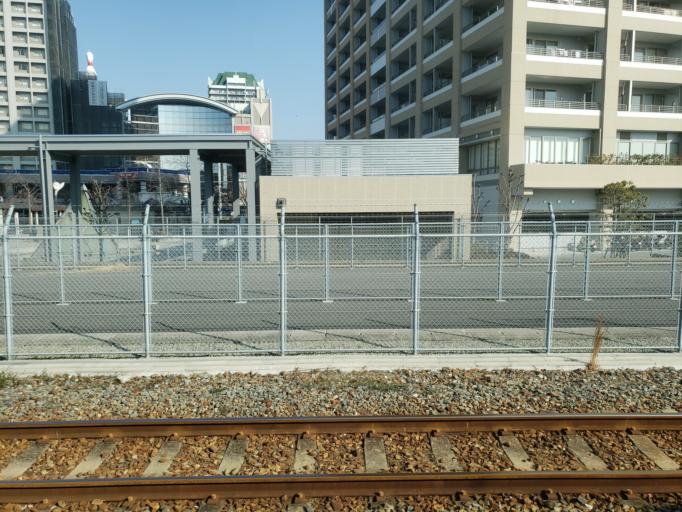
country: JP
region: Hyogo
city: Amagasaki
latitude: 34.7321
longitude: 135.4328
